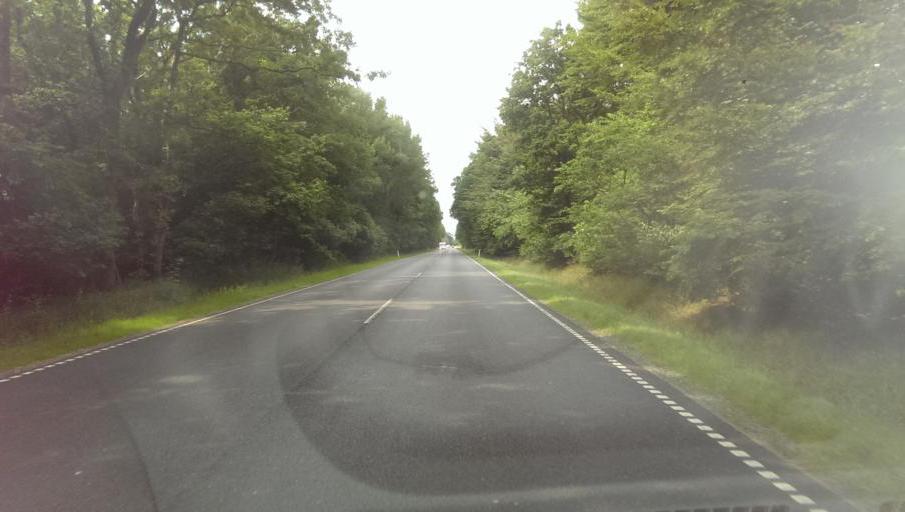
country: DK
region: South Denmark
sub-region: Varde Kommune
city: Varde
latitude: 55.5901
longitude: 8.5143
